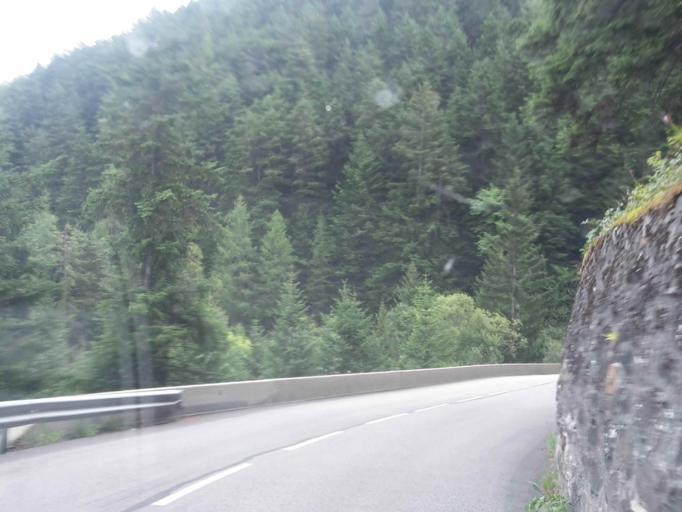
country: FR
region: Rhone-Alpes
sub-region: Departement de la Savoie
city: Saint-Michel-de-Maurienne
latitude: 45.1948
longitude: 6.4569
